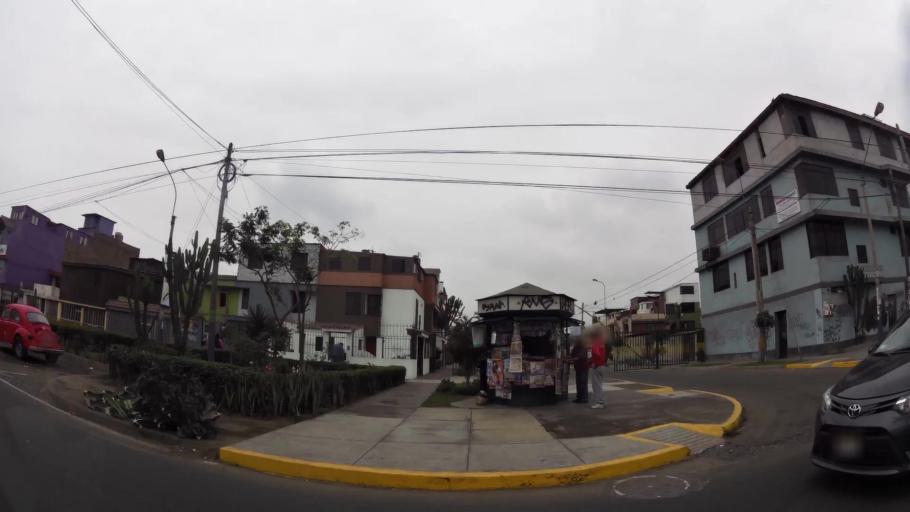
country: PE
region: Lima
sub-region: Lima
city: San Luis
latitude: -12.0804
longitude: -77.0032
